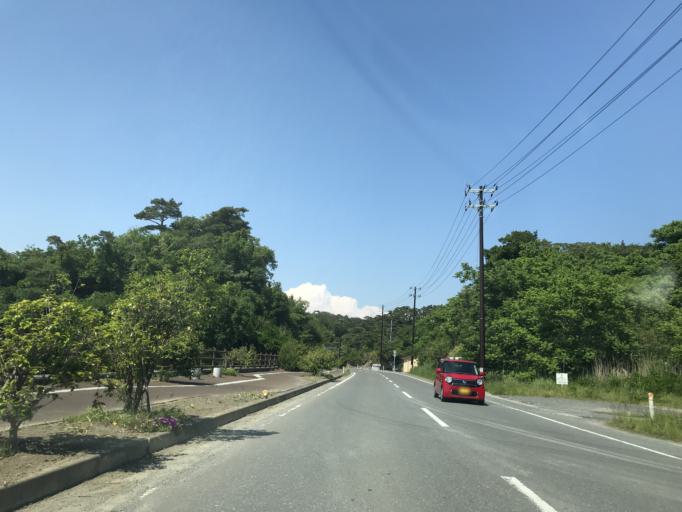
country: JP
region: Miyagi
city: Matsushima
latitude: 38.3405
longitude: 141.1486
